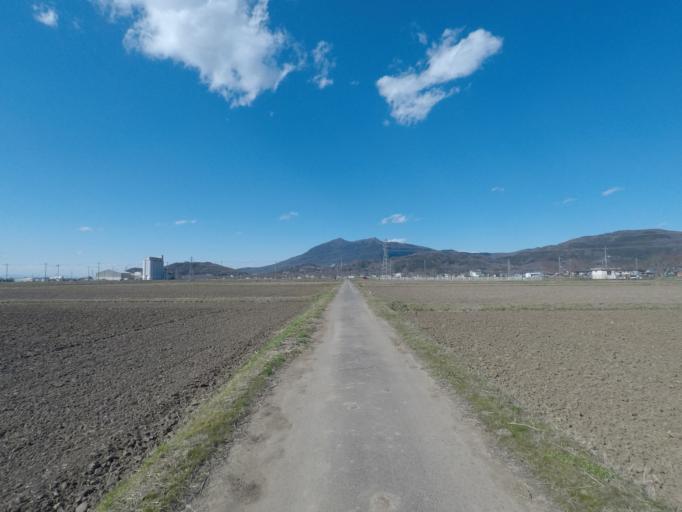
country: JP
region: Ibaraki
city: Tsukuba
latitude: 36.1614
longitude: 140.1014
